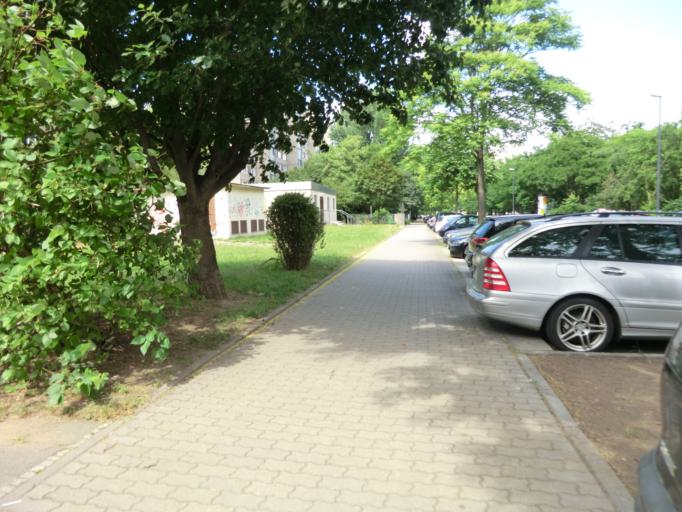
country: DE
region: Saxony
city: Dresden
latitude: 51.0347
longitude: 13.7331
